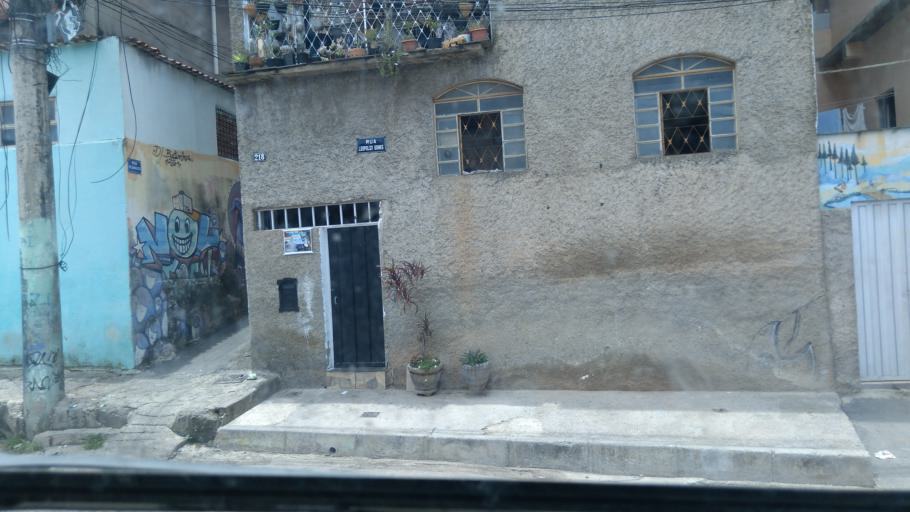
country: BR
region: Minas Gerais
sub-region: Belo Horizonte
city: Belo Horizonte
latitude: -19.9126
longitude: -43.9064
